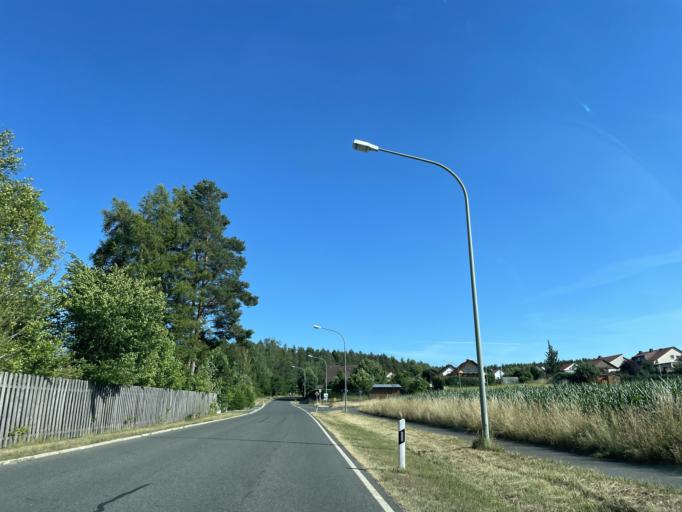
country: DE
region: Bavaria
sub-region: Upper Palatinate
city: Trabitz
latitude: 49.7978
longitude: 11.9012
